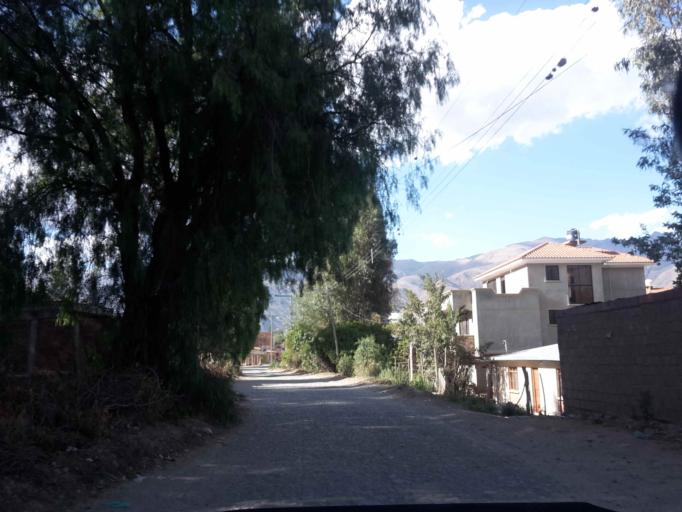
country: BO
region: Cochabamba
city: Cochabamba
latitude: -17.3688
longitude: -66.2077
